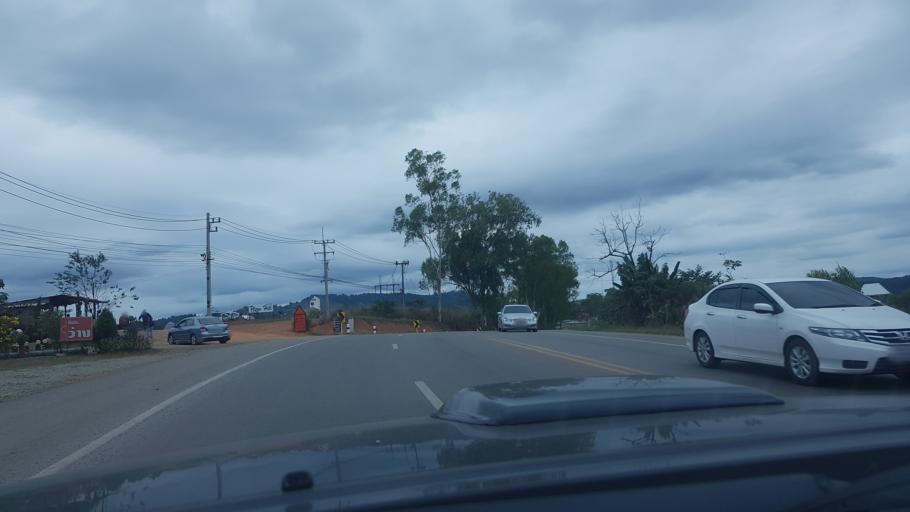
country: TH
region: Phetchabun
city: Khao Kho
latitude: 16.5655
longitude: 101.0074
